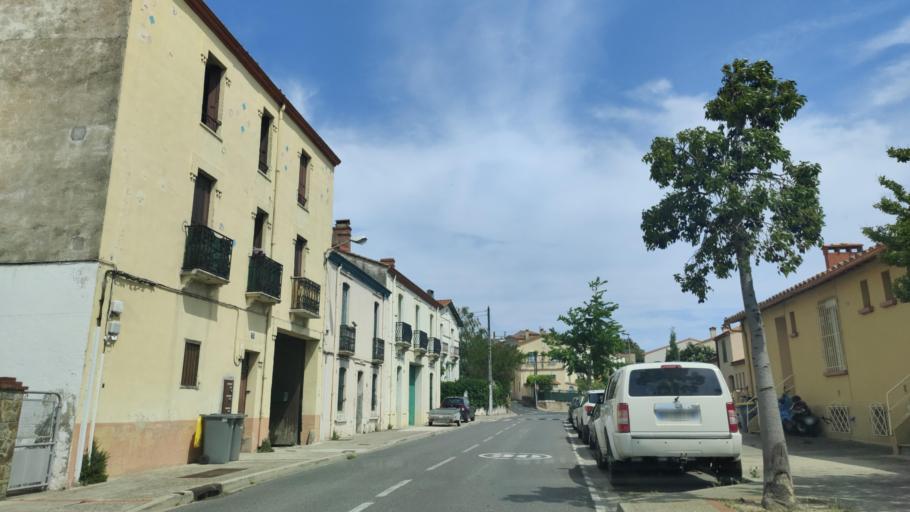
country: FR
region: Languedoc-Roussillon
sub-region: Departement des Pyrenees-Orientales
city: Elne
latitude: 42.5988
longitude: 2.9669
